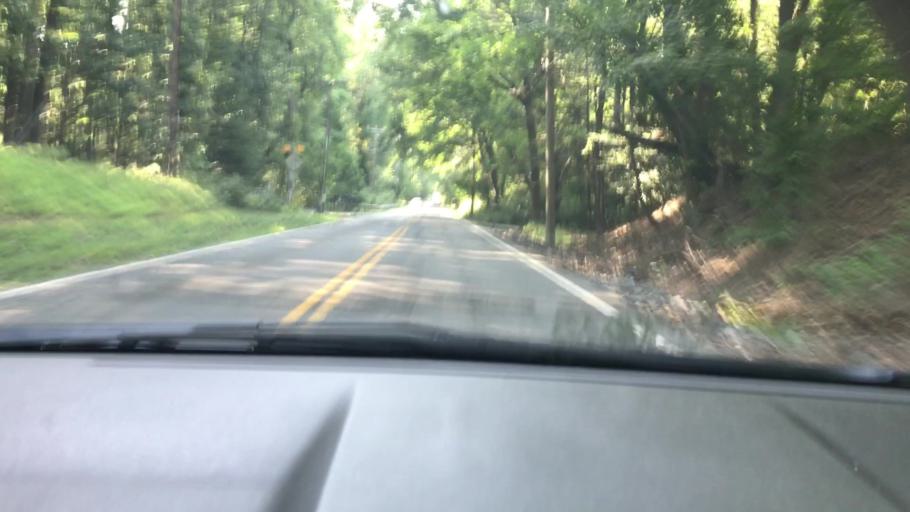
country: US
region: Virginia
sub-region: Fairfax County
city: Tysons Corner
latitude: 38.9618
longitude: -77.2410
